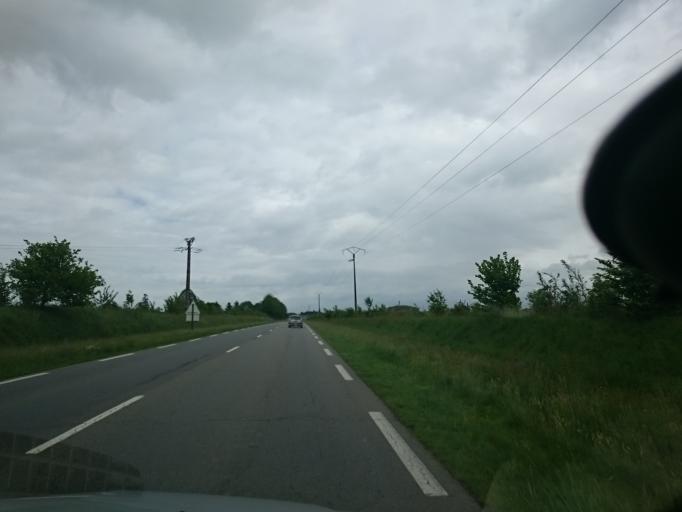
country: FR
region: Brittany
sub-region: Departement d'Ille-et-Vilaine
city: Tremblay
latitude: 48.4242
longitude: -1.4457
